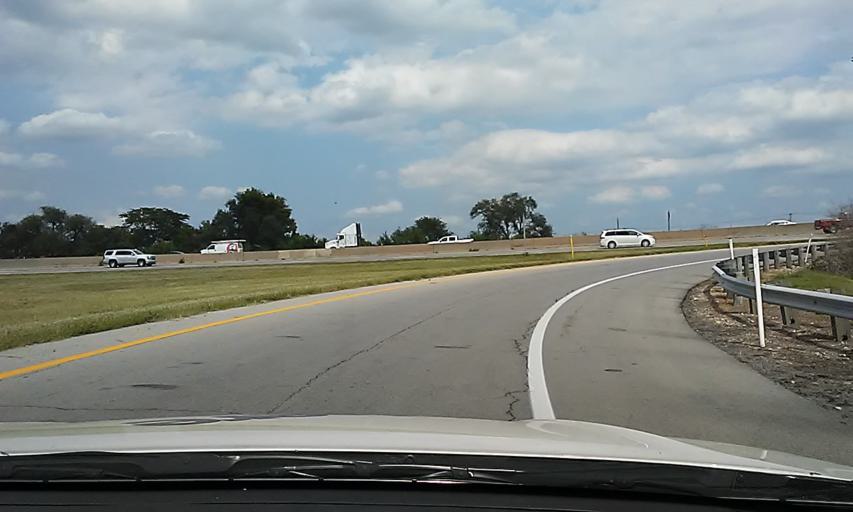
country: US
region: Ohio
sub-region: Montgomery County
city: Northridge
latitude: 39.7893
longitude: -84.1851
